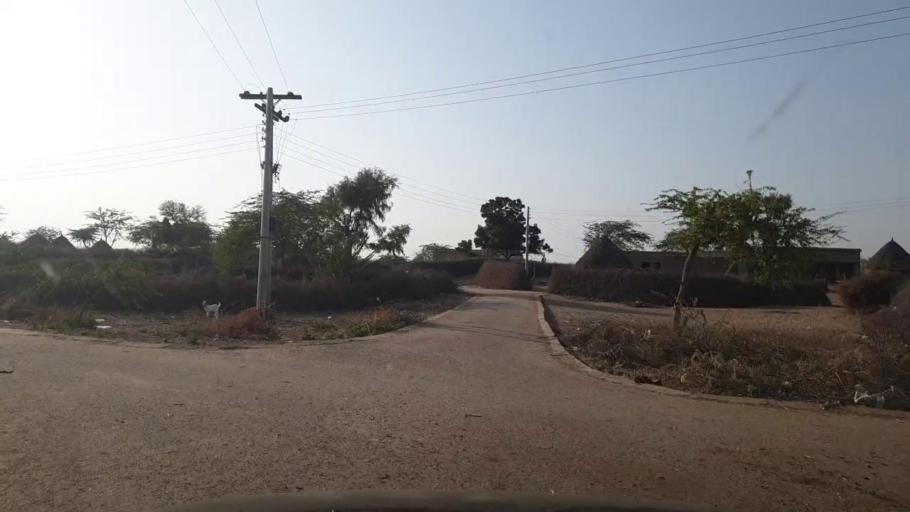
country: PK
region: Sindh
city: Islamkot
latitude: 25.0987
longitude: 70.3667
